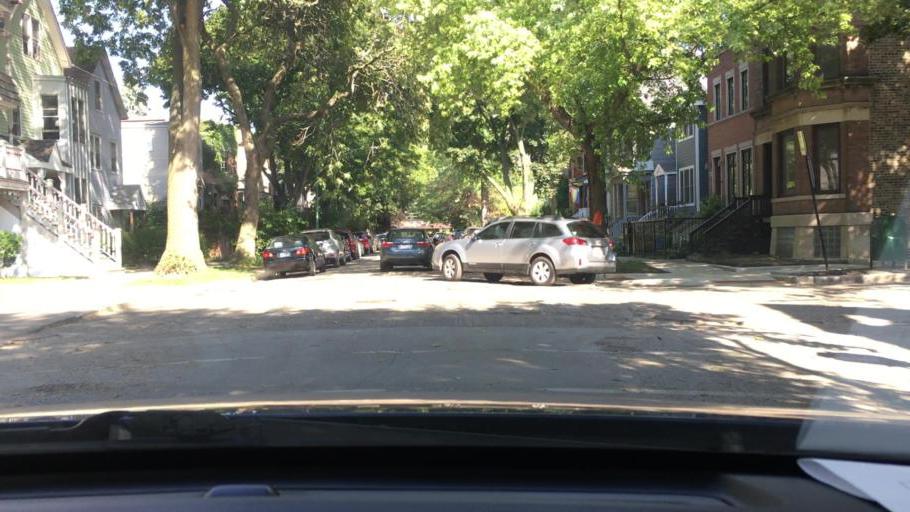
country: US
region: Illinois
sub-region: Cook County
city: Lincolnwood
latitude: 41.9414
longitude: -87.6762
